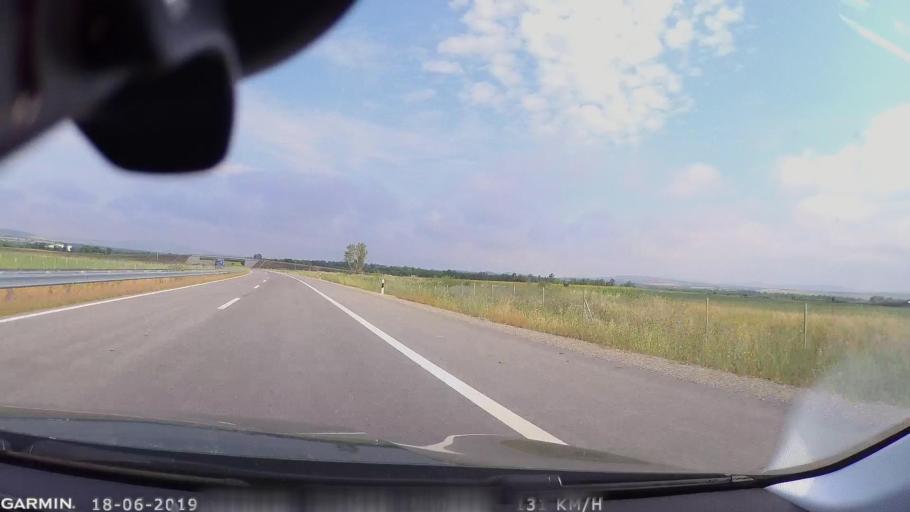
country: MK
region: Sveti Nikole
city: Sveti Nikole
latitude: 41.8247
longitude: 22.0095
